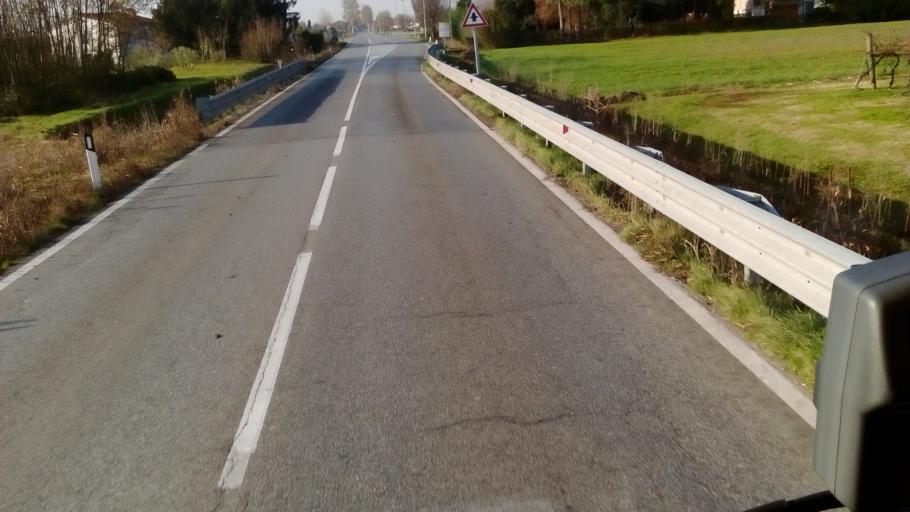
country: IT
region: Friuli Venezia Giulia
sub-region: Provincia di Udine
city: Palazzolo dello Stella
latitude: 45.8111
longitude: 13.1052
